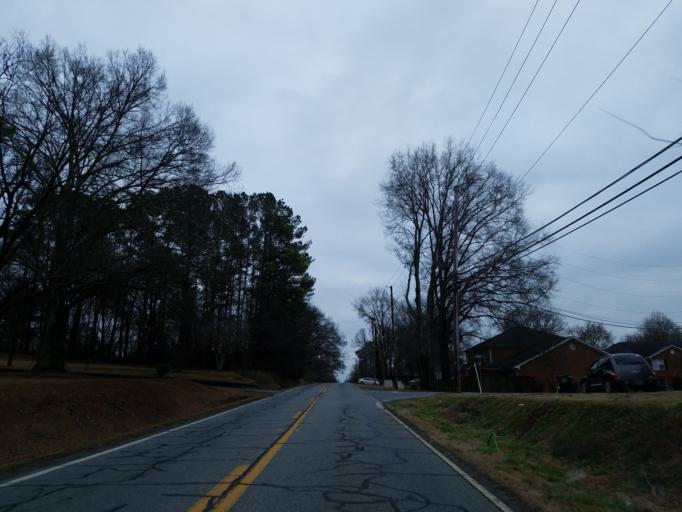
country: US
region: Georgia
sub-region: Bartow County
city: Cartersville
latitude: 34.2086
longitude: -84.8328
